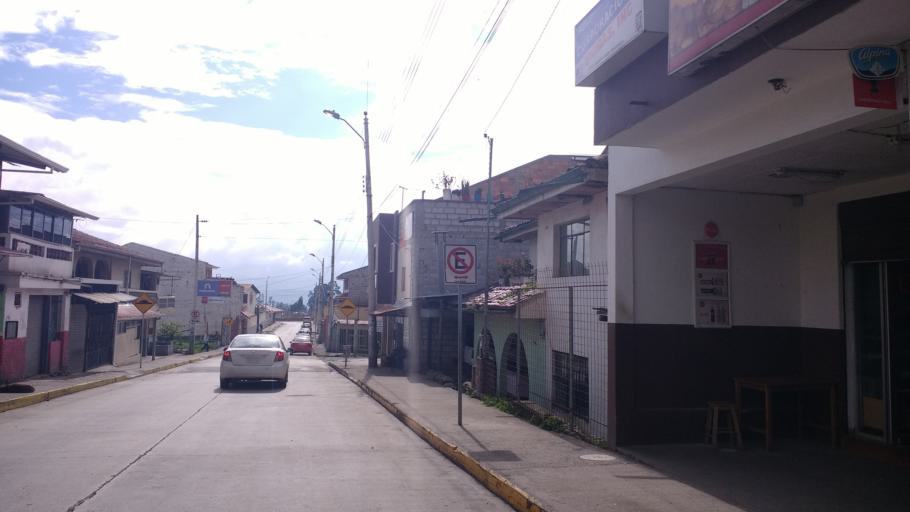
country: EC
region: Azuay
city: Cuenca
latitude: -2.8963
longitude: -79.0513
